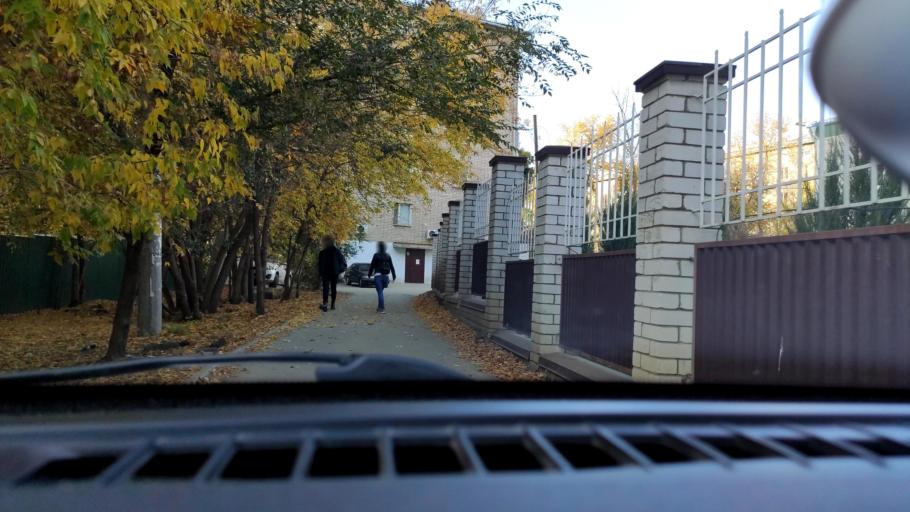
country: RU
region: Samara
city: Samara
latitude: 53.1926
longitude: 50.1367
